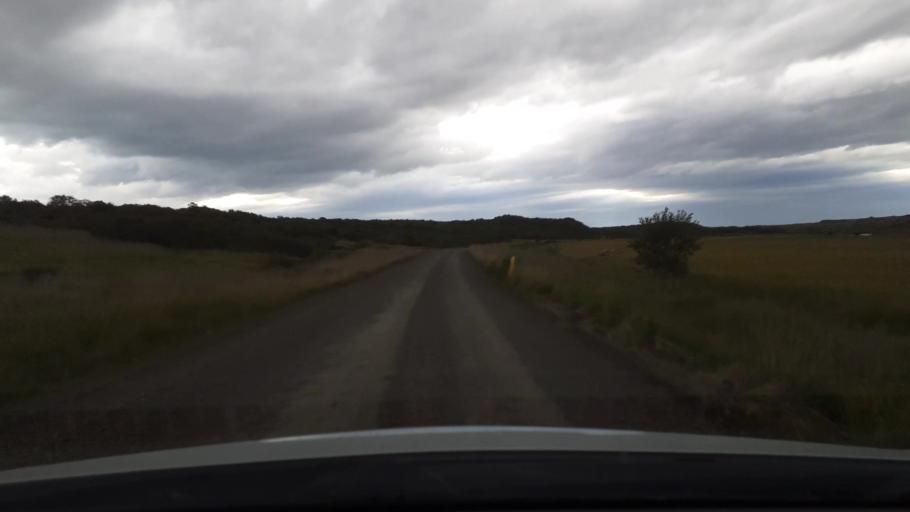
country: IS
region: West
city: Borgarnes
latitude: 64.6111
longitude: -21.9535
